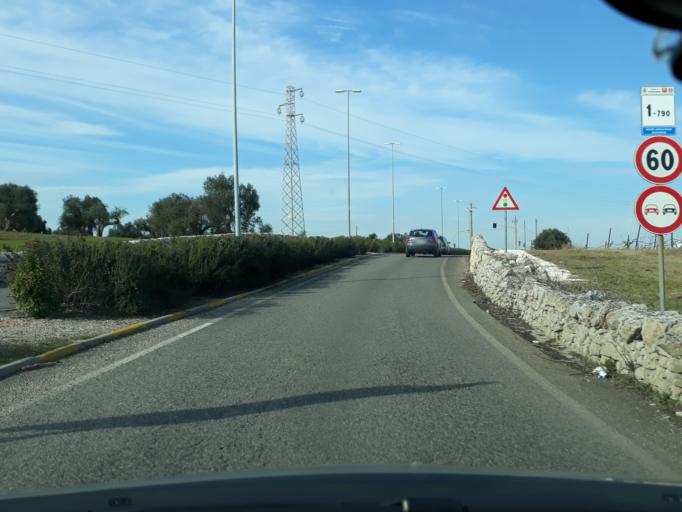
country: IT
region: Apulia
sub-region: Provincia di Bari
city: Locorotondo
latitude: 40.7547
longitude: 17.3441
